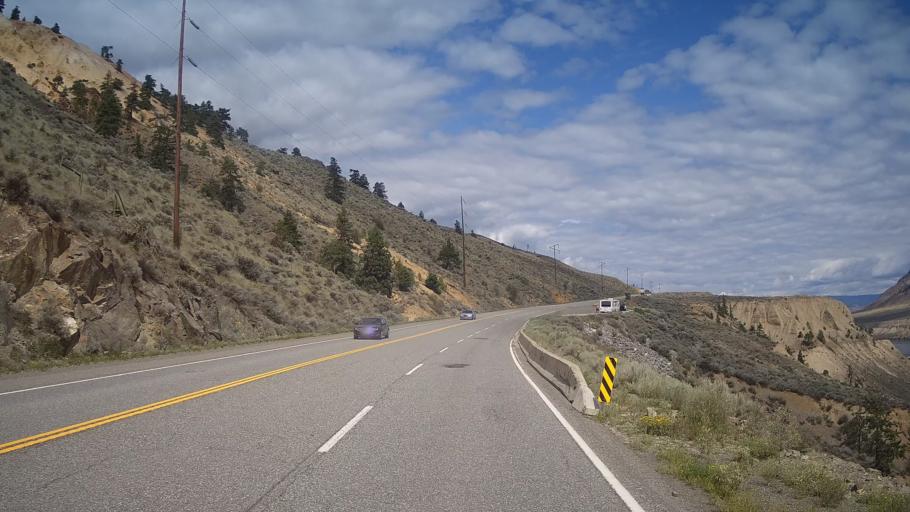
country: CA
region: British Columbia
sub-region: Thompson-Nicola Regional District
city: Ashcroft
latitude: 50.5554
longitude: -121.3004
